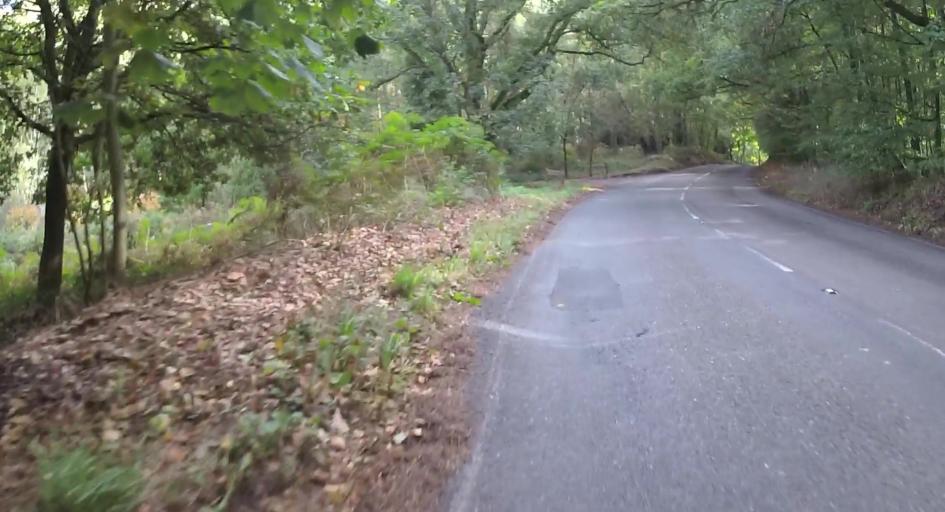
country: GB
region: England
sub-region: Surrey
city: Seale
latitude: 51.2042
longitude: -0.7449
